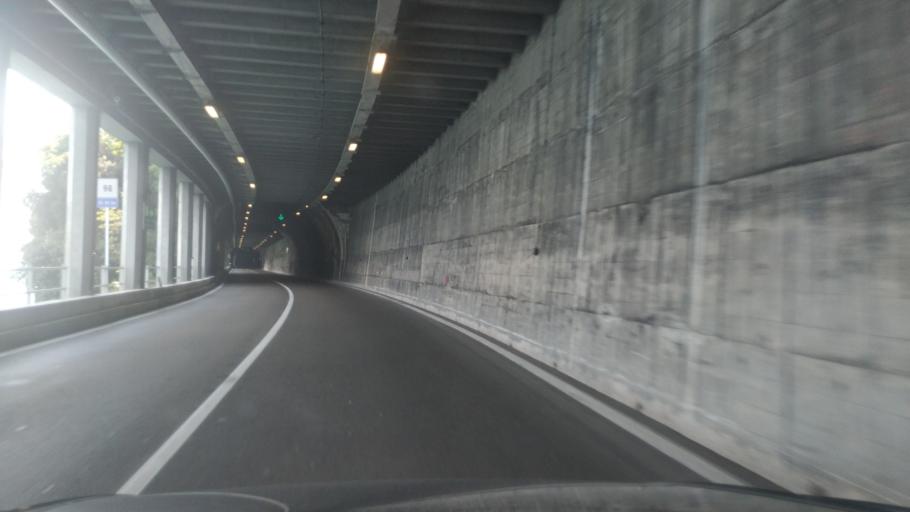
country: IT
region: Lombardy
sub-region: Provincia di Brescia
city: Pieve
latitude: 45.7773
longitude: 10.7705
